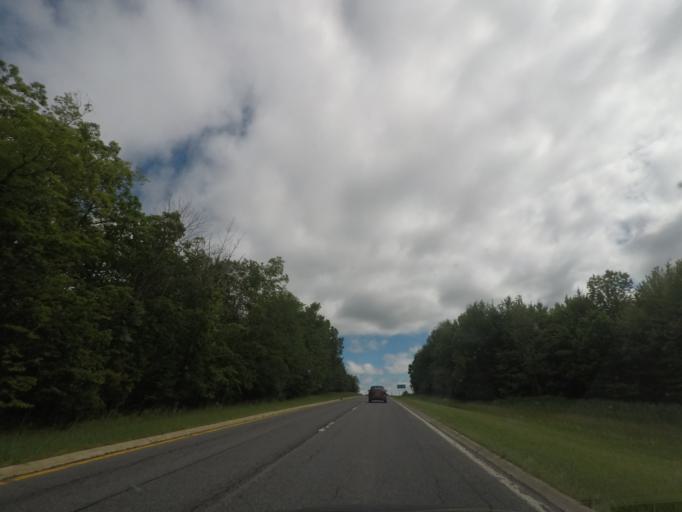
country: US
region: New York
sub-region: Columbia County
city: Philmont
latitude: 42.2656
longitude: -73.6143
